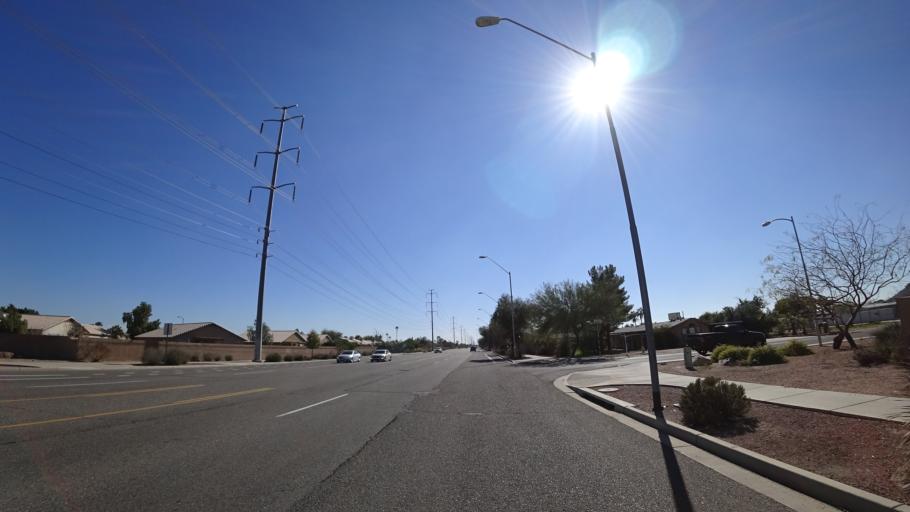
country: US
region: Arizona
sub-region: Maricopa County
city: Peoria
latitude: 33.6824
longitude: -112.1349
